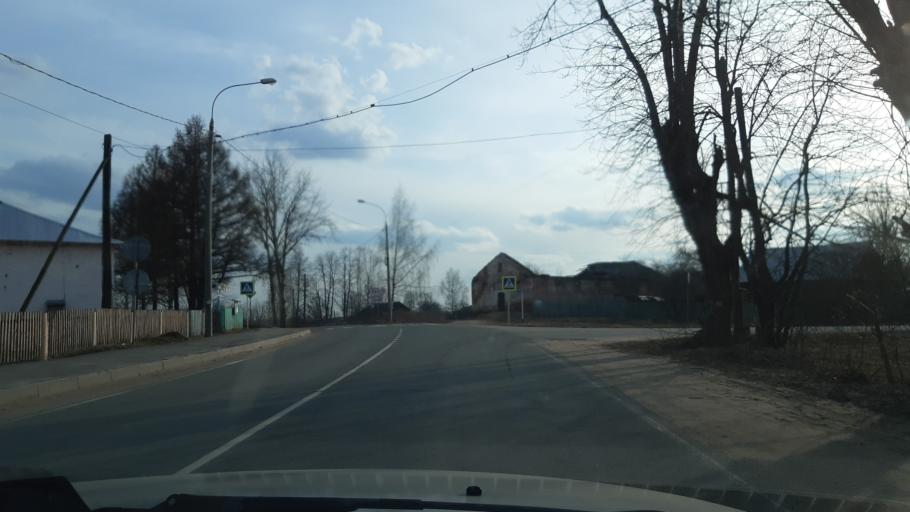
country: RU
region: Vladimir
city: Nikologory
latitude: 56.1474
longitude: 41.9935
